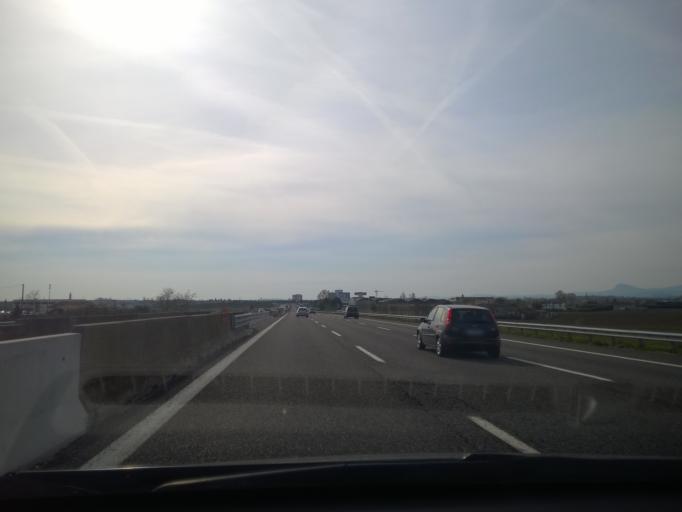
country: IT
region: Emilia-Romagna
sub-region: Forli-Cesena
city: Gatteo-Sant'Angelo
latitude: 44.1274
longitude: 12.3794
